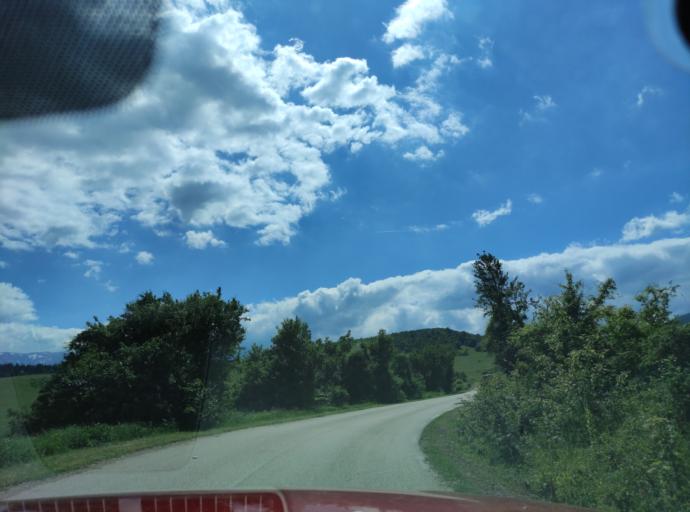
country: BG
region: Vidin
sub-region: Obshtina Ruzhintsi
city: Ruzhintsi
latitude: 43.5006
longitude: 22.7718
